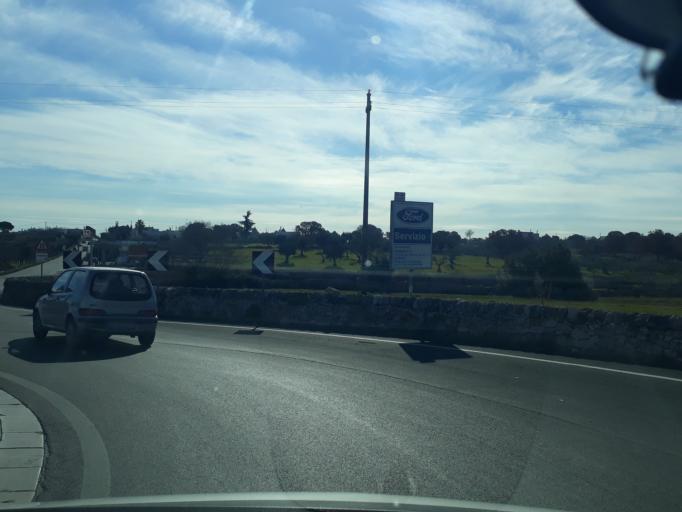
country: IT
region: Apulia
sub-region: Provincia di Bari
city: Locorotondo
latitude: 40.7492
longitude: 17.3293
